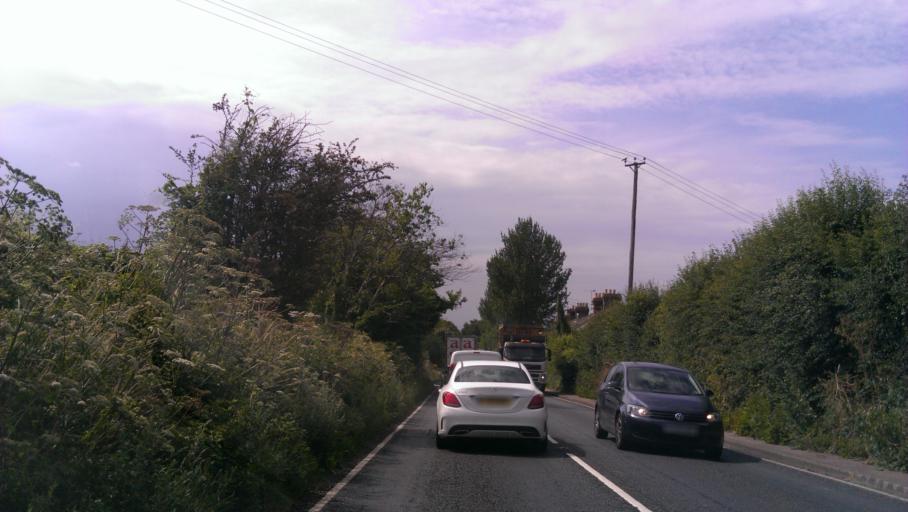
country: GB
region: England
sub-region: Kent
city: Teynham
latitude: 51.3244
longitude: 0.8134
